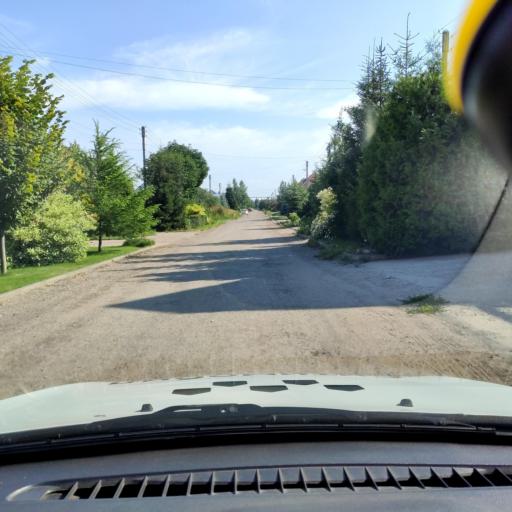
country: RU
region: Samara
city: Podstepki
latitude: 53.5202
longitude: 49.1903
